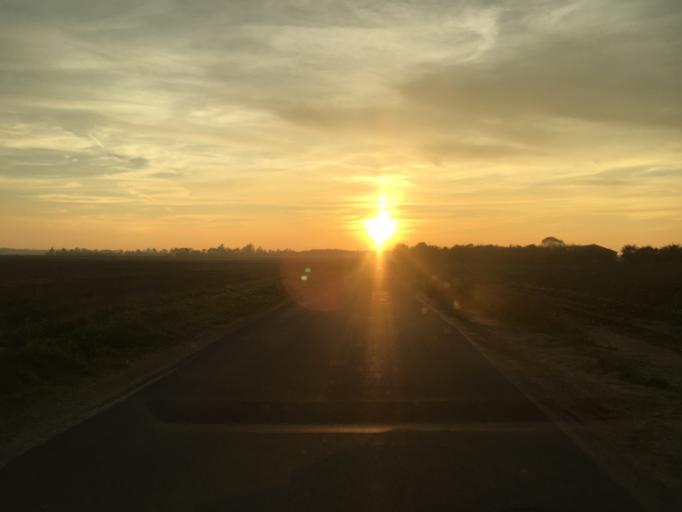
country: DK
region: South Denmark
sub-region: Tonder Kommune
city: Logumkloster
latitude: 55.0168
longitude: 9.0967
